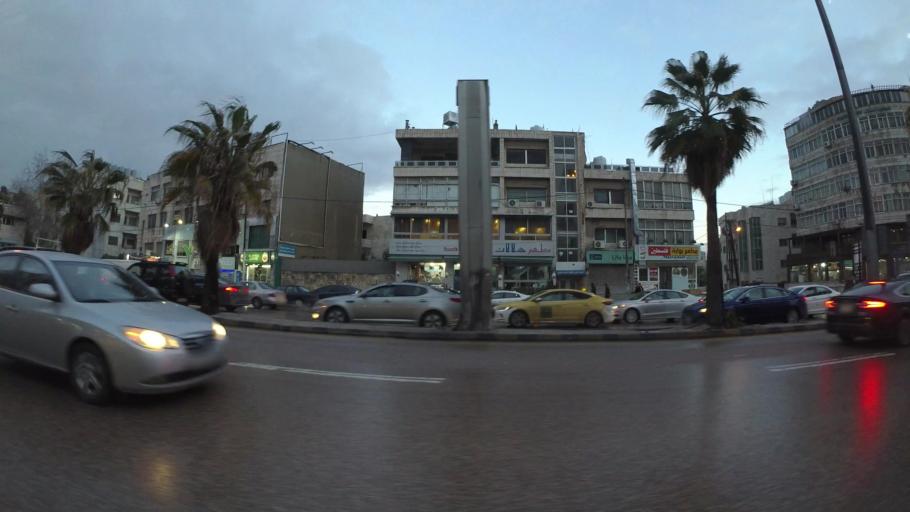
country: JO
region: Amman
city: Al Jubayhah
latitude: 31.9838
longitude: 35.8955
